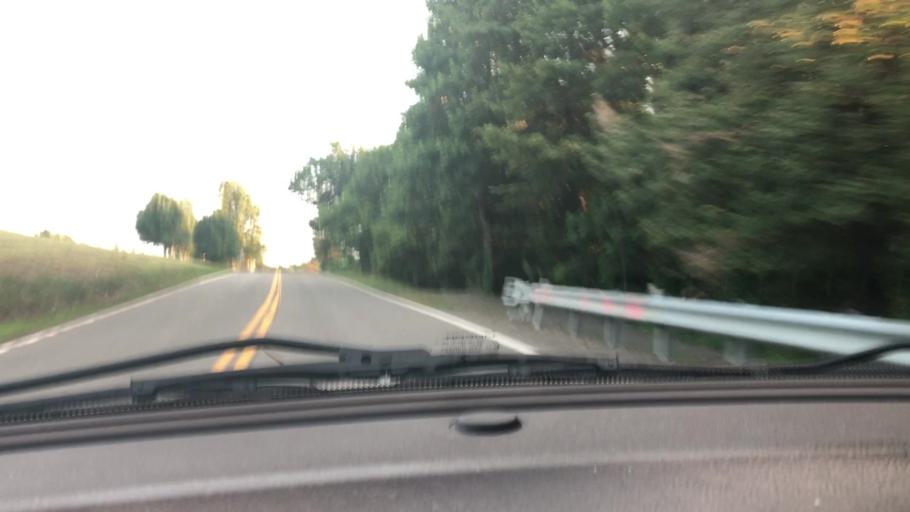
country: US
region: Virginia
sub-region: Patrick County
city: Stuart
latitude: 36.7202
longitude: -80.3331
